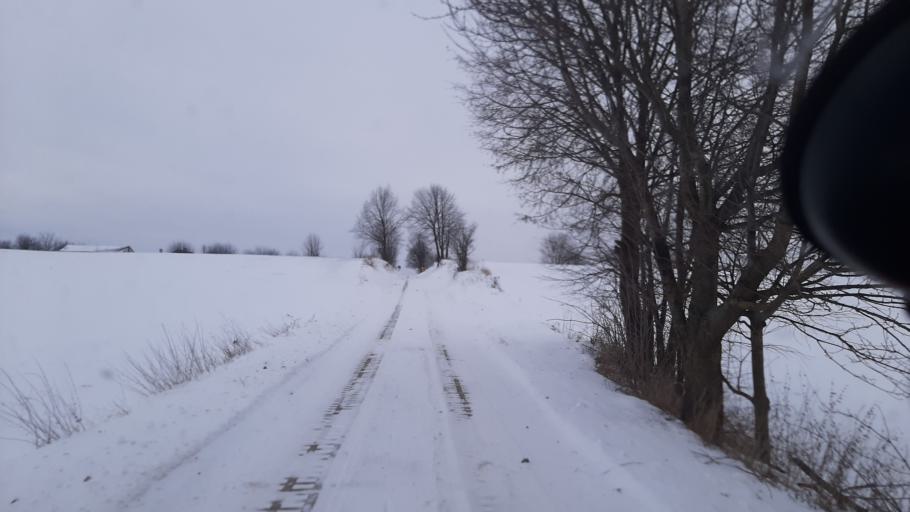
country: PL
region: Lublin Voivodeship
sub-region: Powiat lubelski
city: Garbow
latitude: 51.3310
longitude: 22.2949
